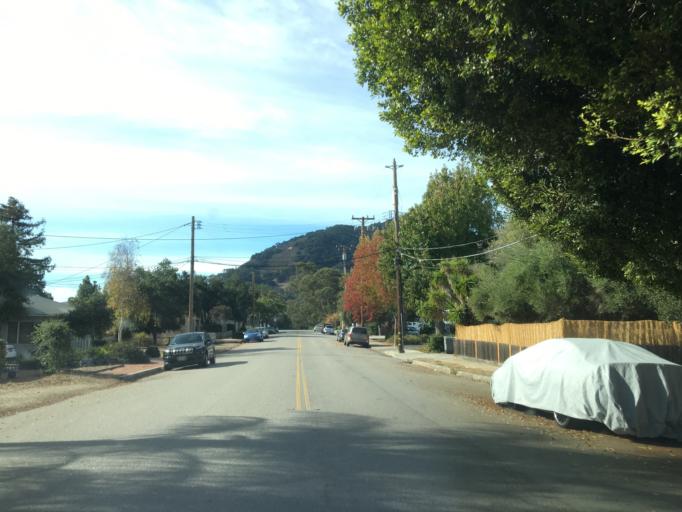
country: US
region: California
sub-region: San Luis Obispo County
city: San Luis Obispo
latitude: 35.2890
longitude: -120.6637
